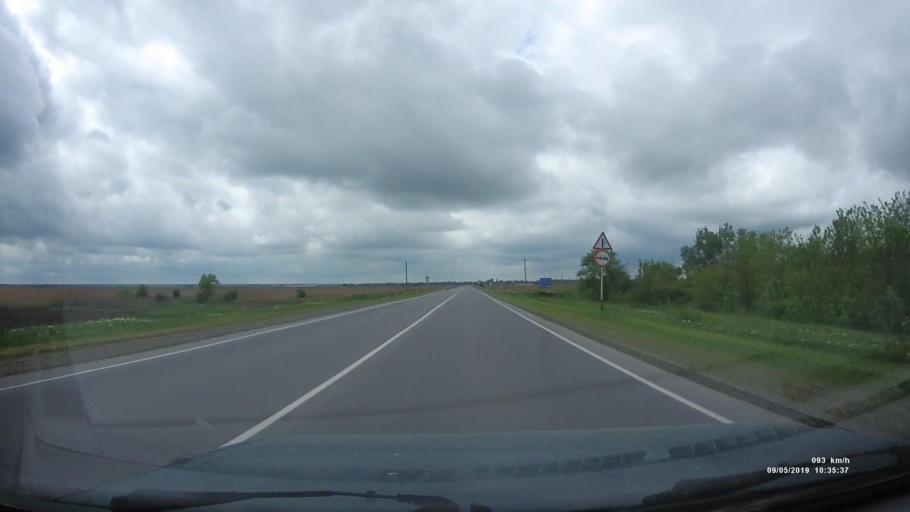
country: RU
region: Rostov
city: Peshkovo
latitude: 47.0404
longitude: 39.4128
